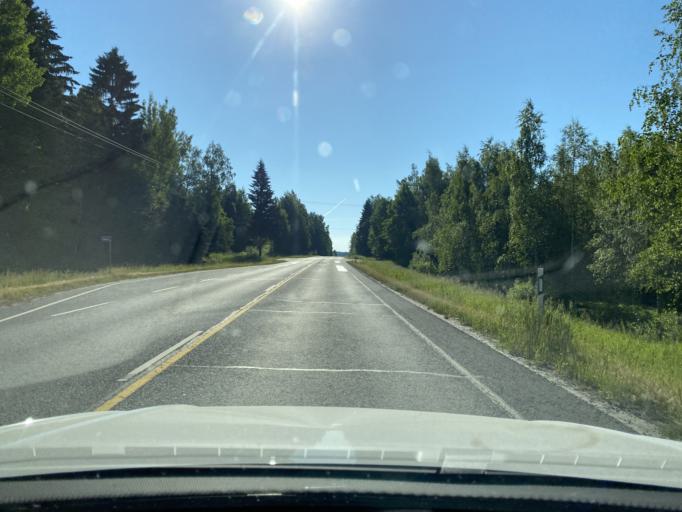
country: FI
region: Haeme
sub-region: Forssa
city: Tammela
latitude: 60.8270
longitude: 23.9290
